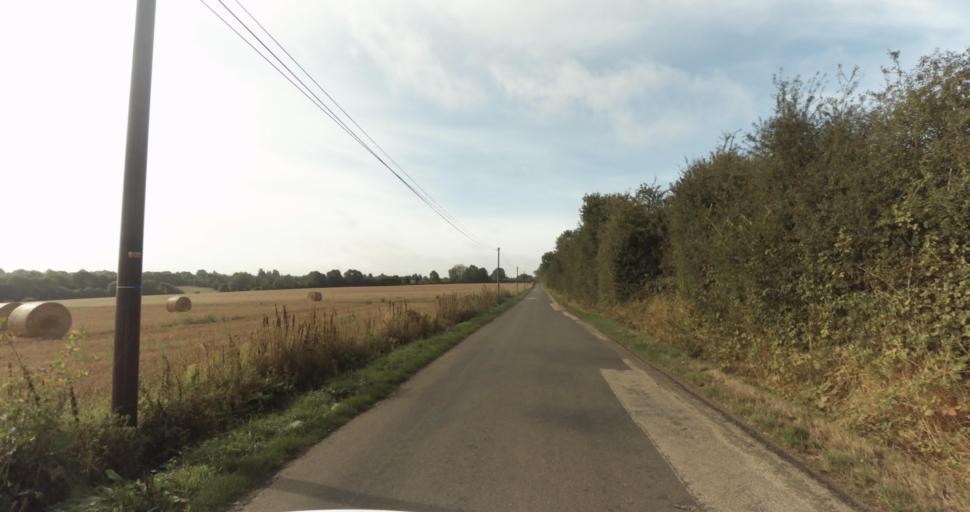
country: FR
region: Lower Normandy
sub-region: Departement de l'Orne
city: Gace
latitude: 48.9033
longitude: 0.3393
